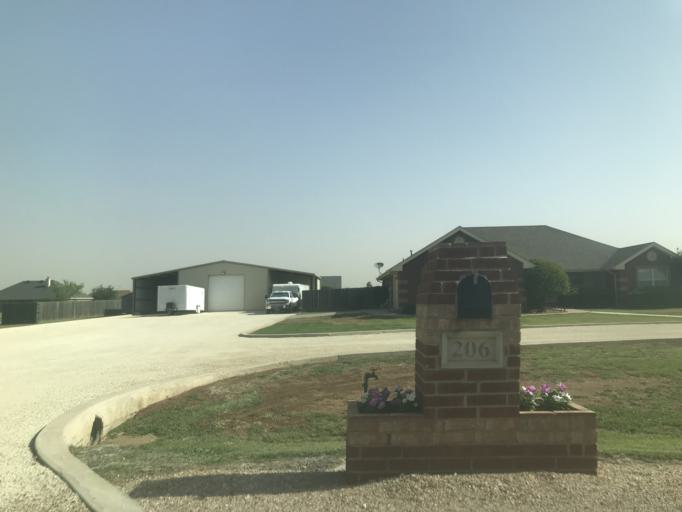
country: US
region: Texas
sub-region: Taylor County
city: Potosi
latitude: 32.3387
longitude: -99.7148
